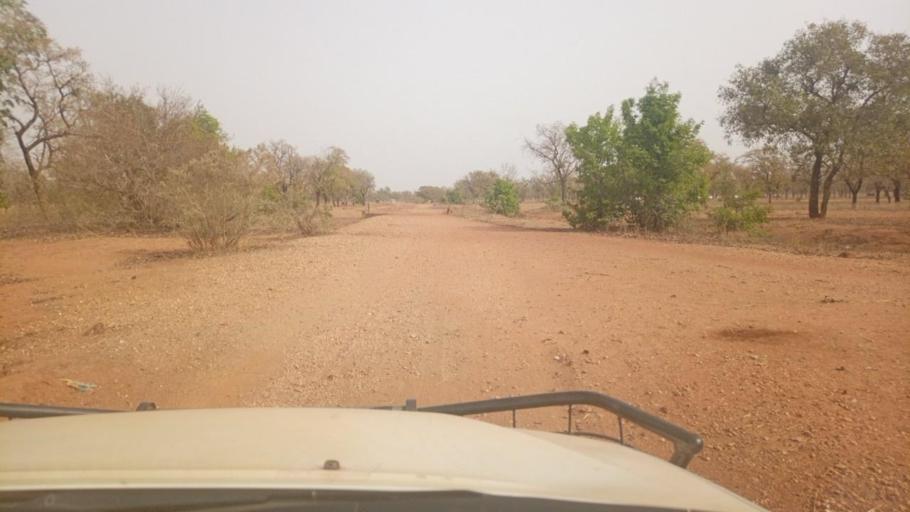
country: BF
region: Boucle du Mouhoun
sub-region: Province des Banwa
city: Salanso
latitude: 12.0959
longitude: -4.3310
